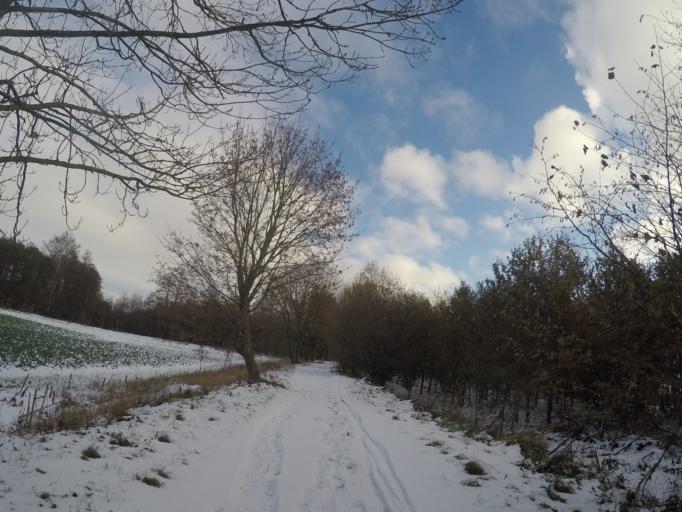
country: SE
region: Skane
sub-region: Lunds Kommun
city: Lund
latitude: 55.7853
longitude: 13.2228
